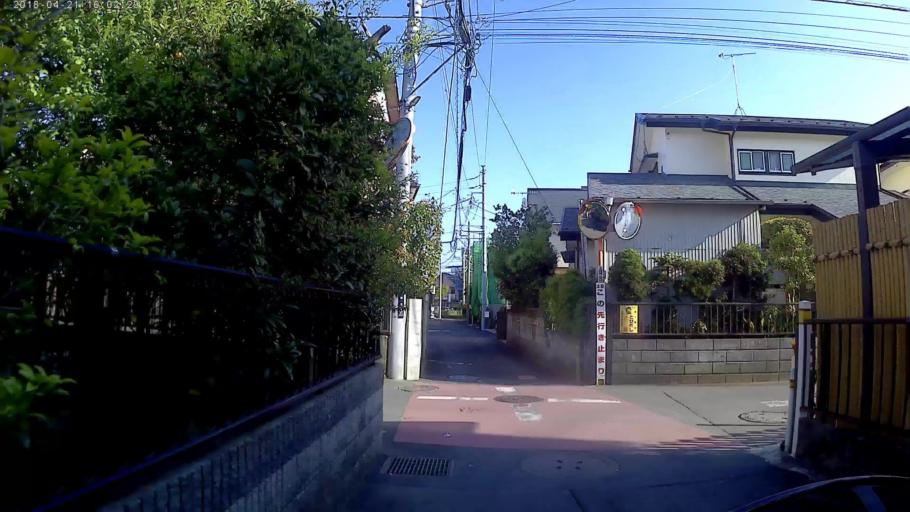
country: JP
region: Kanagawa
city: Fujisawa
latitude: 35.3372
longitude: 139.4382
